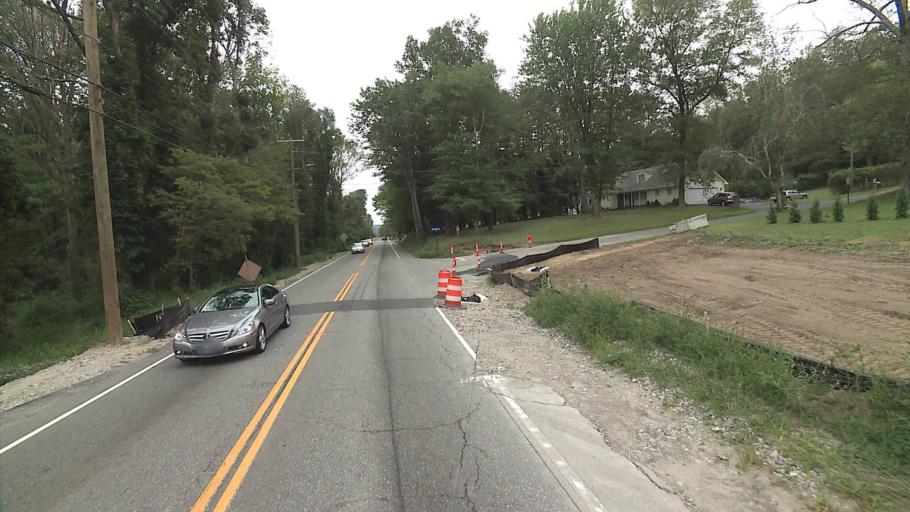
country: US
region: Connecticut
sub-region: New London County
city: Montville Center
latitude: 41.4521
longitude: -72.2368
